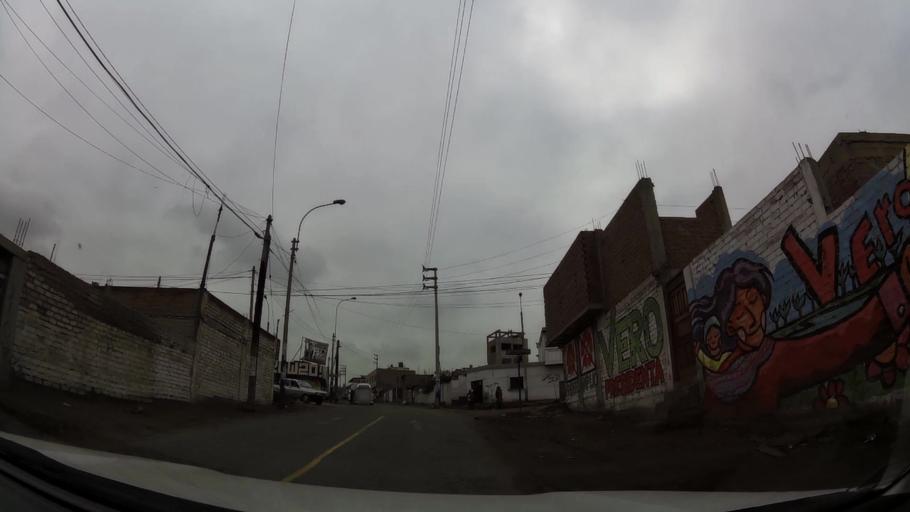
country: PE
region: Lima
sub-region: Lima
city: Surco
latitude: -12.2013
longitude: -76.9912
